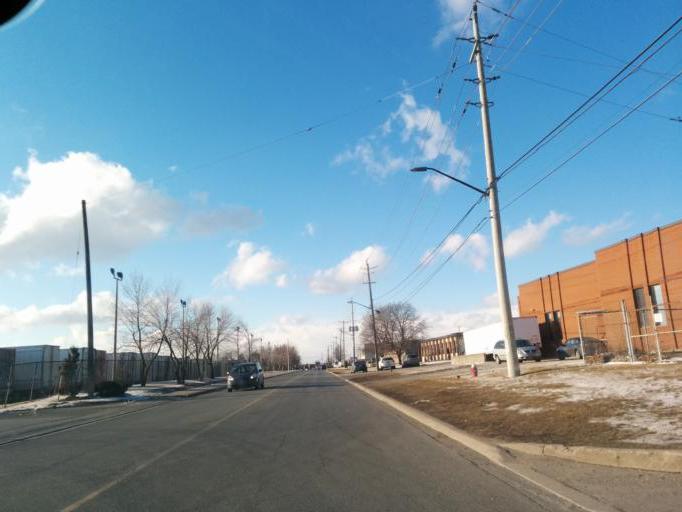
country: CA
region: Ontario
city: Mississauga
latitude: 43.6315
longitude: -79.6289
